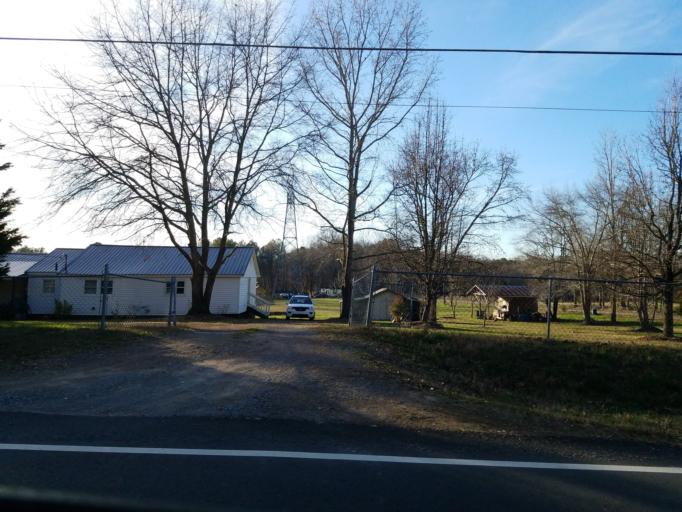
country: US
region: Georgia
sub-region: Gordon County
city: Calhoun
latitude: 34.5422
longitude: -84.9738
